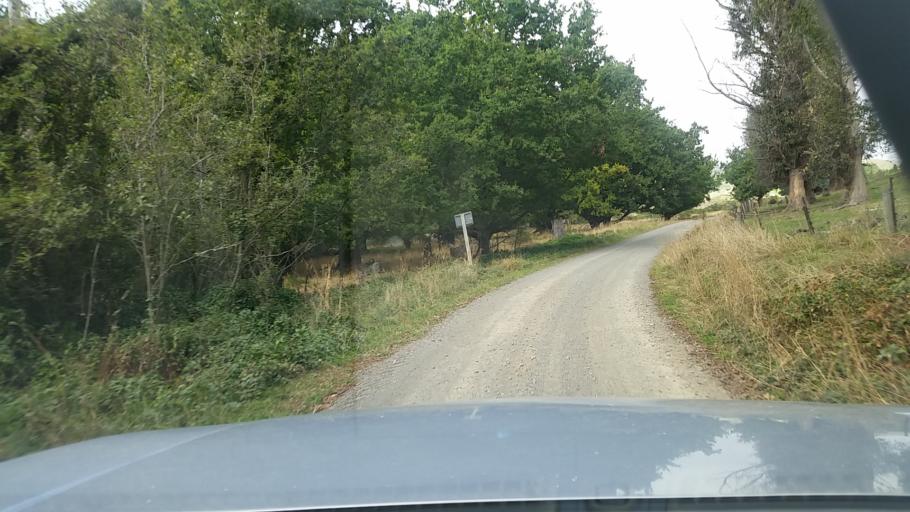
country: NZ
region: Marlborough
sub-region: Marlborough District
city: Blenheim
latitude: -41.7366
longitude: 173.8925
